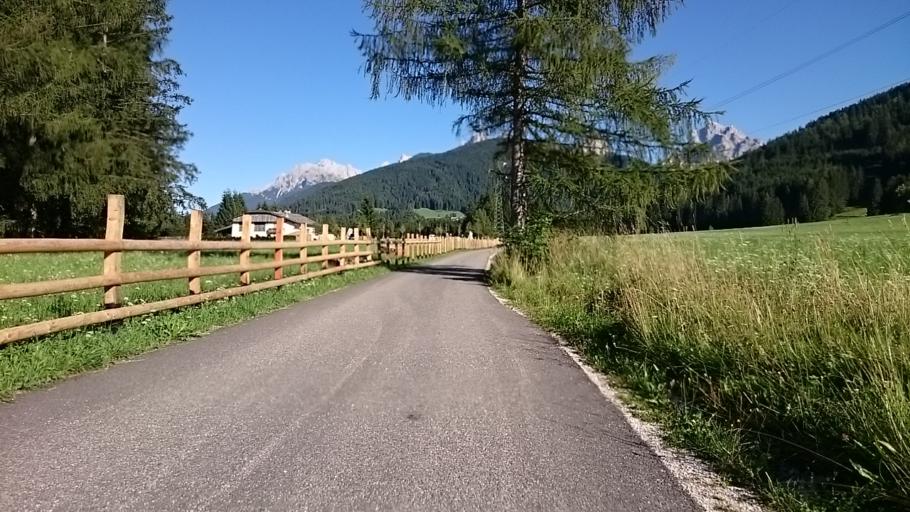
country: IT
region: Trentino-Alto Adige
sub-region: Bolzano
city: Monguelfo
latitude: 46.7436
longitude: 12.1242
